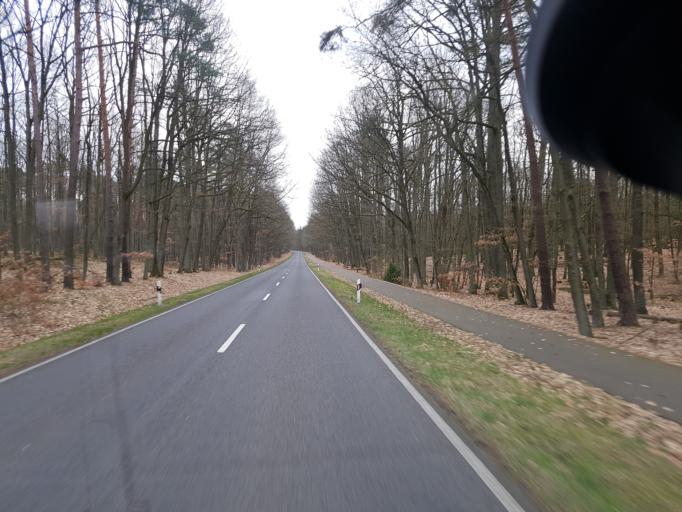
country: DE
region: Brandenburg
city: Gross Lindow
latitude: 52.1788
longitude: 14.4780
